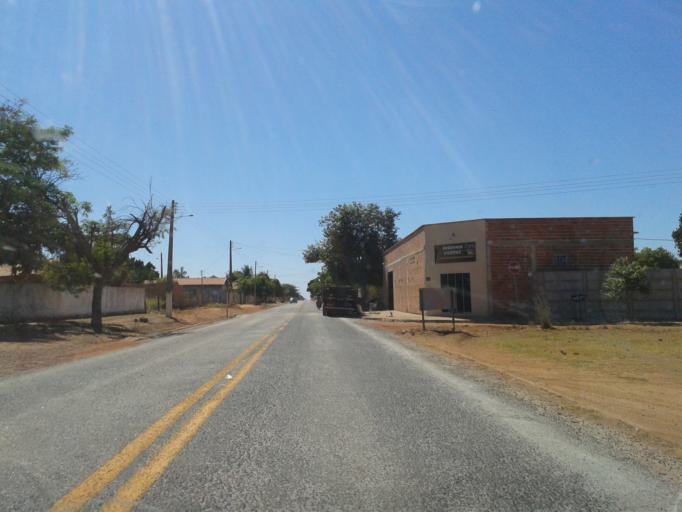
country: BR
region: Goias
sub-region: Sao Miguel Do Araguaia
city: Sao Miguel do Araguaia
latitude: -13.2654
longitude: -50.1517
